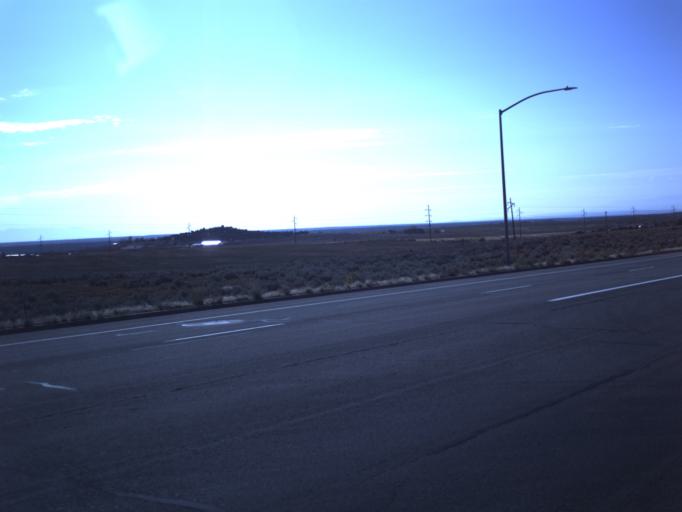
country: US
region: Utah
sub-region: San Juan County
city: Blanding
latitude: 37.6030
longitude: -109.4788
